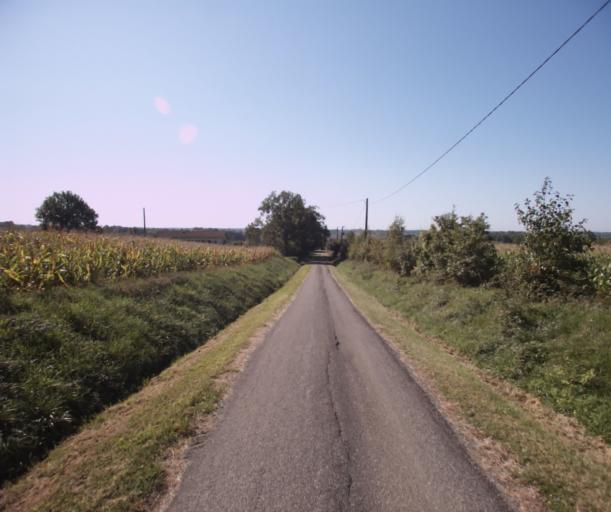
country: FR
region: Aquitaine
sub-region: Departement des Landes
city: Gabarret
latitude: 43.9483
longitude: 0.0036
